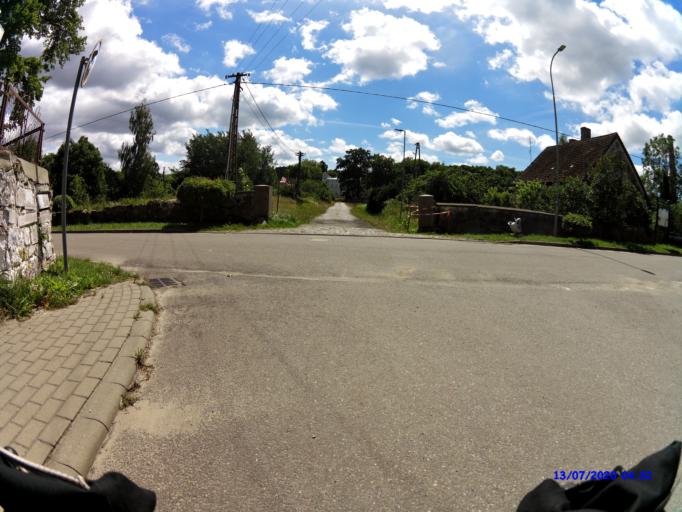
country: PL
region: West Pomeranian Voivodeship
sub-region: Powiat bialogardzki
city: Karlino
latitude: 54.0650
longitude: 15.8387
